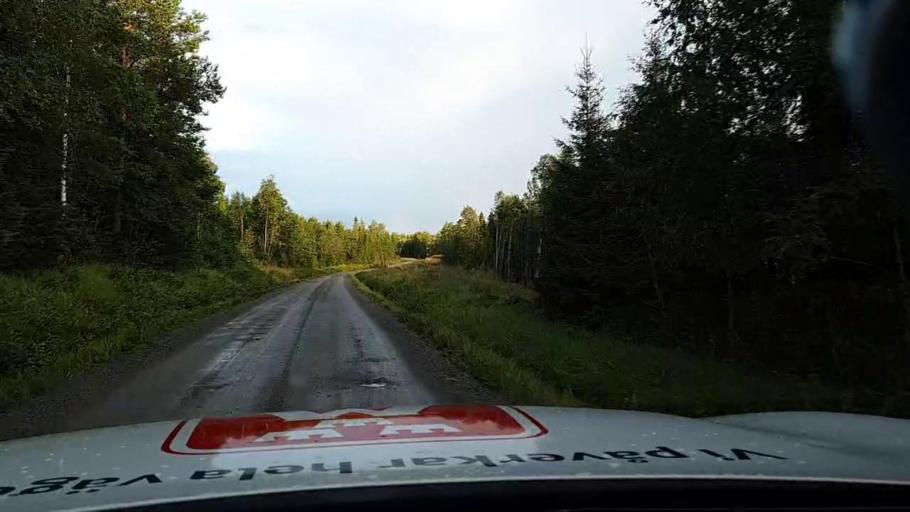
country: SE
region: Jaemtland
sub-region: Bergs Kommun
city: Hoverberg
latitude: 62.8574
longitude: 14.5347
